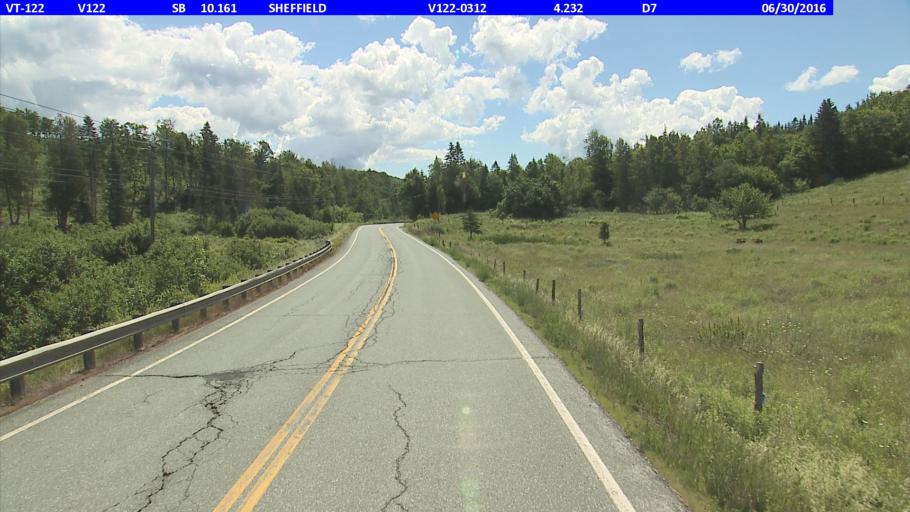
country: US
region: Vermont
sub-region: Caledonia County
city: Lyndonville
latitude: 44.6346
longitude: -72.1433
